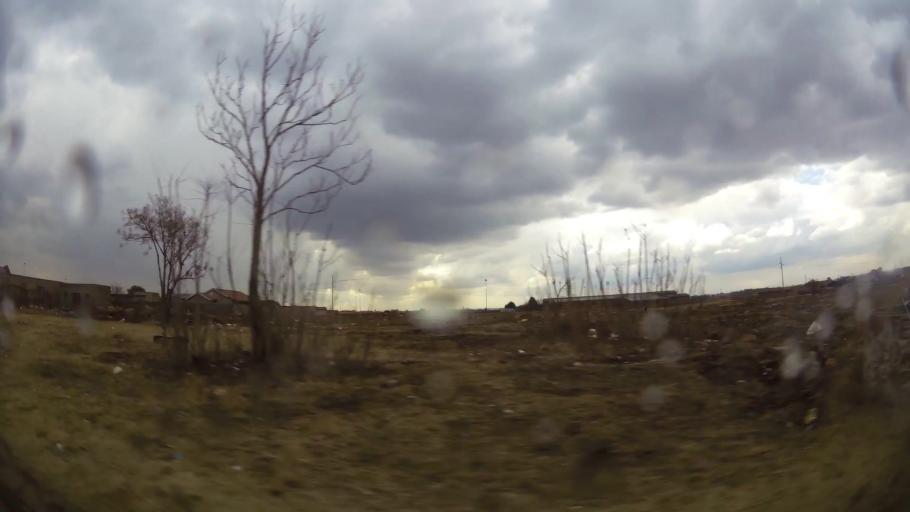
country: ZA
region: Gauteng
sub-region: Ekurhuleni Metropolitan Municipality
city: Germiston
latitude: -26.3605
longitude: 28.1653
